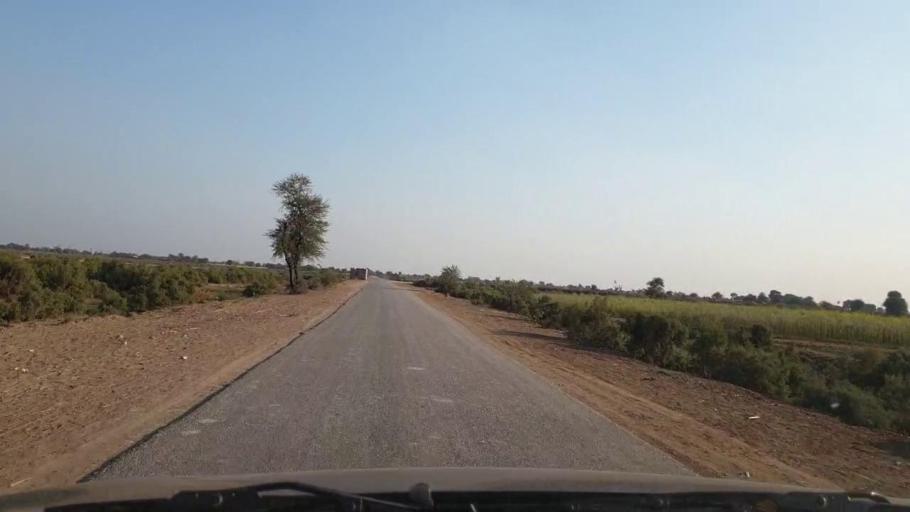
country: PK
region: Sindh
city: Jhol
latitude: 25.9372
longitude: 68.9129
